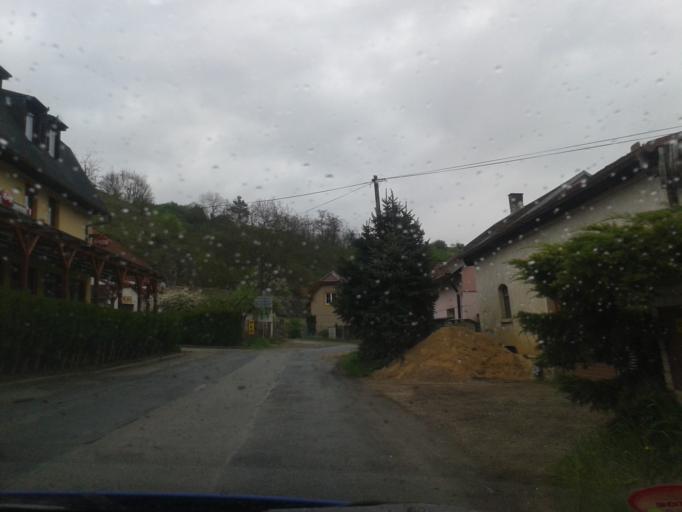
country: CZ
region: Central Bohemia
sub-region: Okres Beroun
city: Lodenice
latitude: 49.9363
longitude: 14.1349
